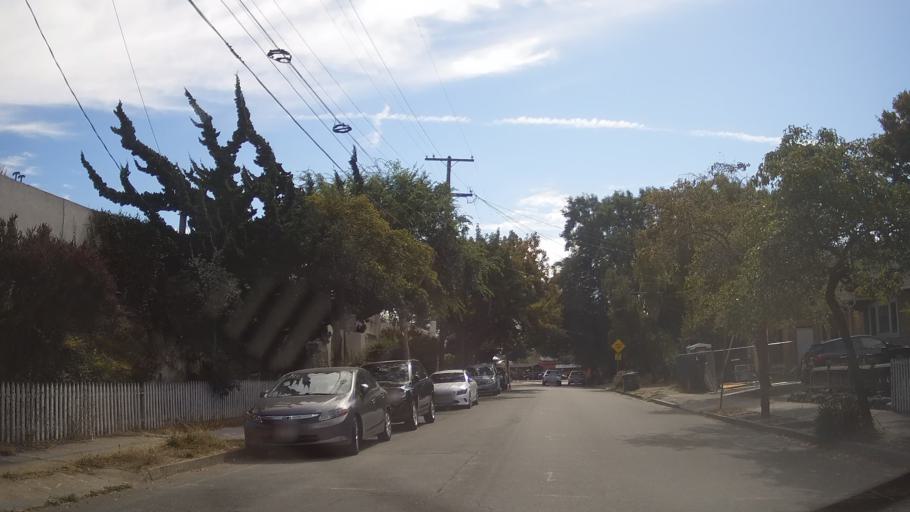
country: US
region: California
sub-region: Alameda County
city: Albany
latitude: 37.8828
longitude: -122.2911
